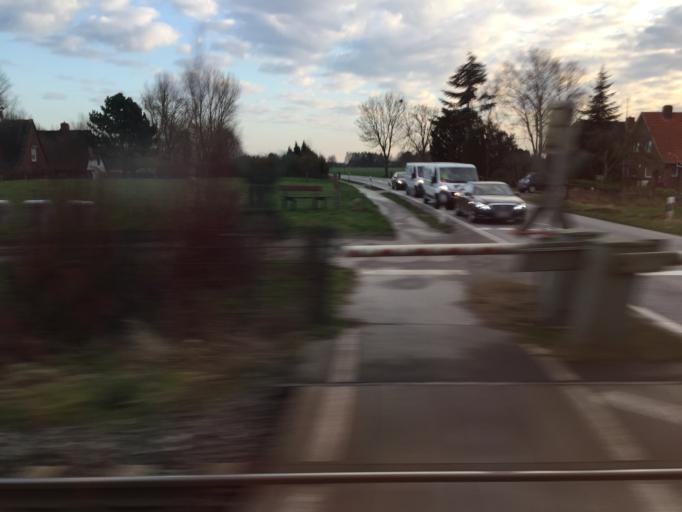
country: DE
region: Schleswig-Holstein
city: Gluckstadt
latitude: 53.8086
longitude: 9.4401
